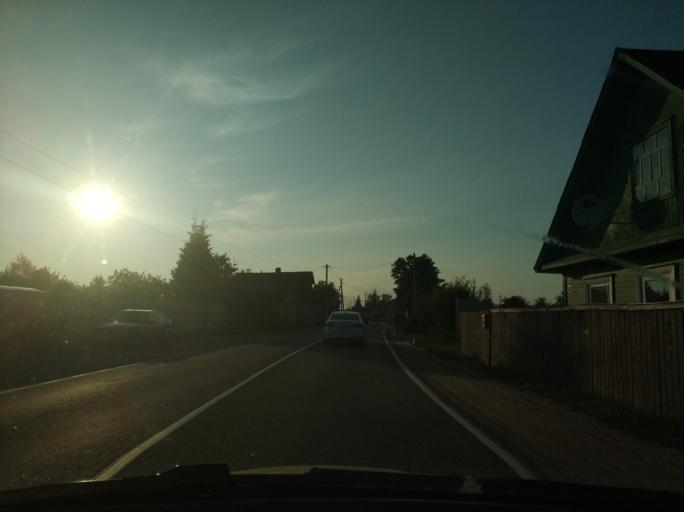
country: RU
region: Leningrad
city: Borisova Griva
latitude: 60.0855
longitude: 31.0244
